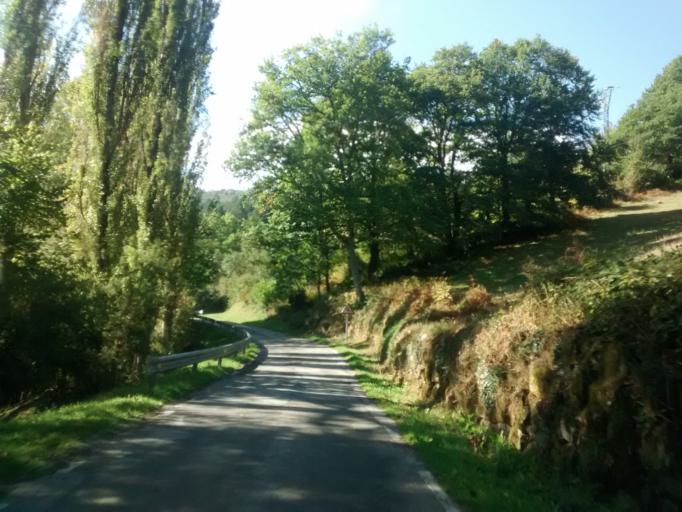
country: ES
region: Cantabria
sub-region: Provincia de Cantabria
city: Reinosa
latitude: 42.9403
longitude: -4.0489
